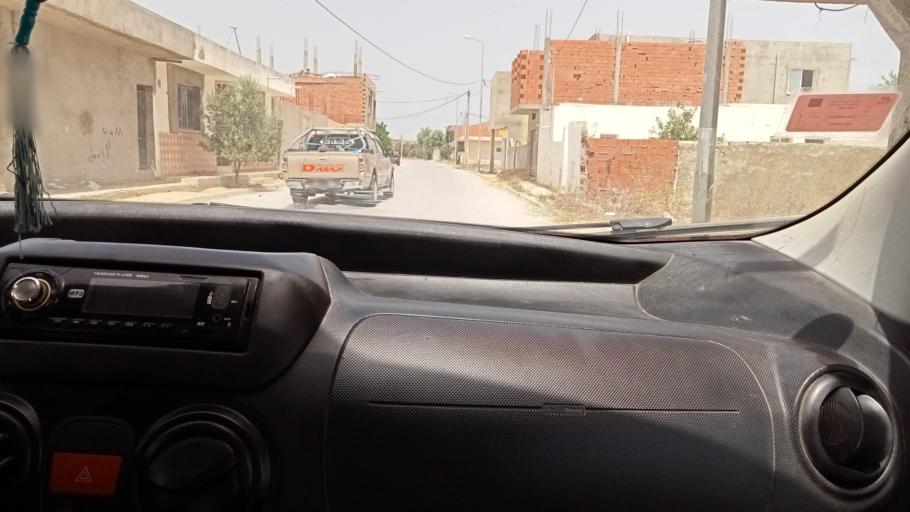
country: TN
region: Nabul
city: Qulaybiyah
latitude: 36.8607
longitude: 11.0876
